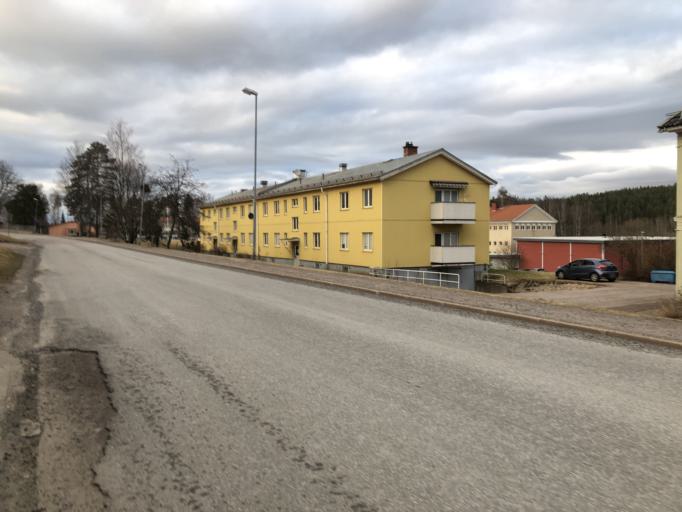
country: SE
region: Vaermland
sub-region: Filipstads Kommun
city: Lesjofors
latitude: 59.9830
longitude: 14.1748
